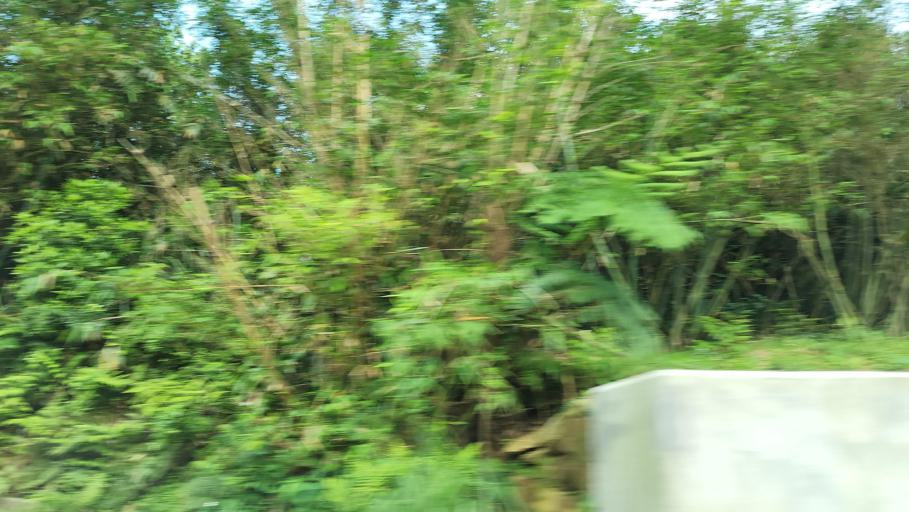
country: TW
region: Taiwan
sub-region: Keelung
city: Keelung
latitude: 25.1858
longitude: 121.6404
